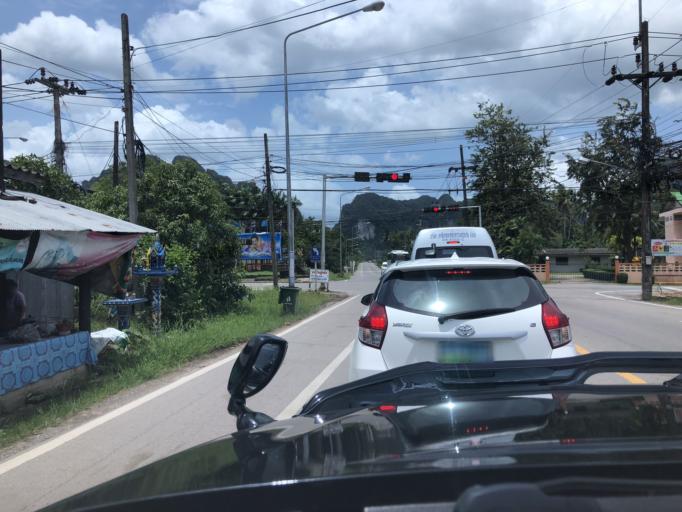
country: TH
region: Krabi
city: Ao Luek
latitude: 8.3787
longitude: 98.7229
